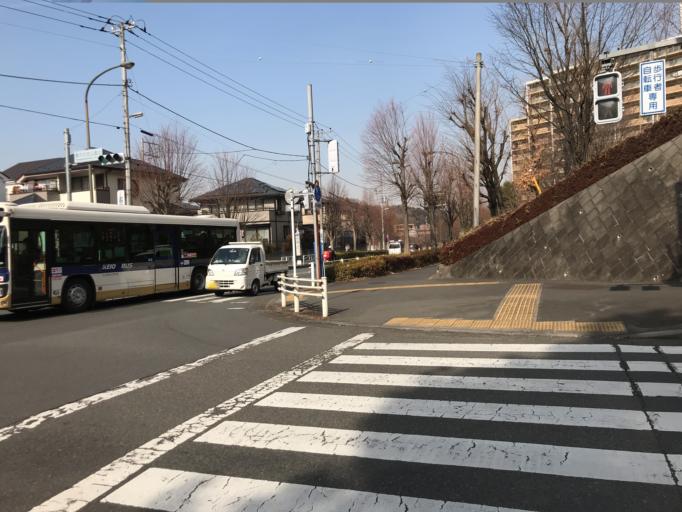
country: JP
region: Tokyo
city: Hino
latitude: 35.6202
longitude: 139.3768
